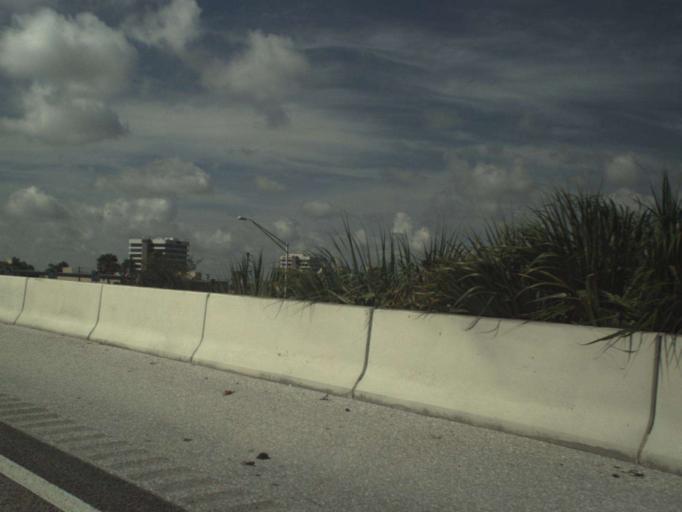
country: US
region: Florida
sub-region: Palm Beach County
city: Schall Circle
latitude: 26.7209
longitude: -80.0910
